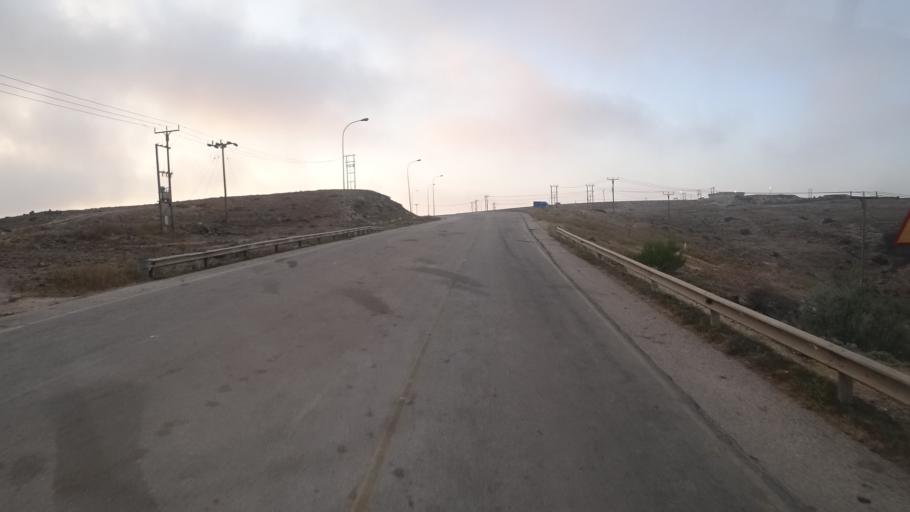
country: OM
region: Zufar
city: Salalah
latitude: 17.1215
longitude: 53.9286
